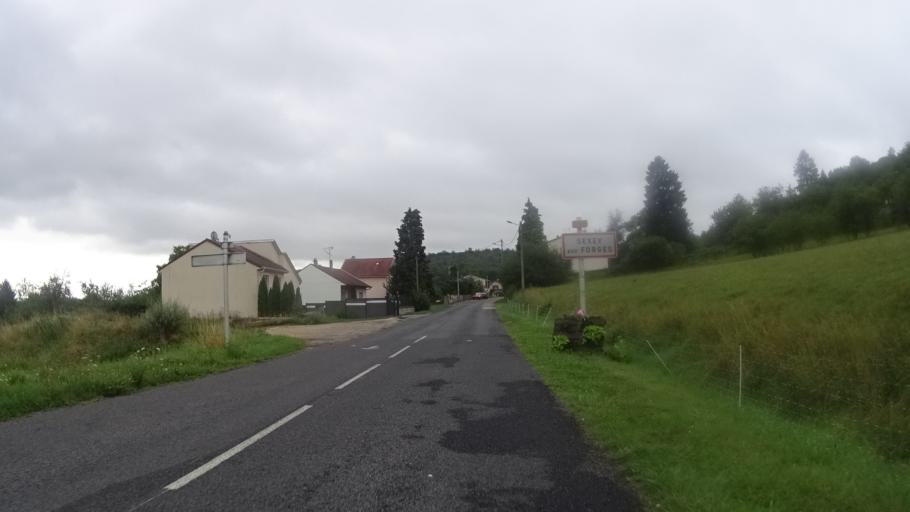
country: FR
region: Lorraine
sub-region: Departement de Meurthe-et-Moselle
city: Chaligny
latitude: 48.6261
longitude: 6.0446
